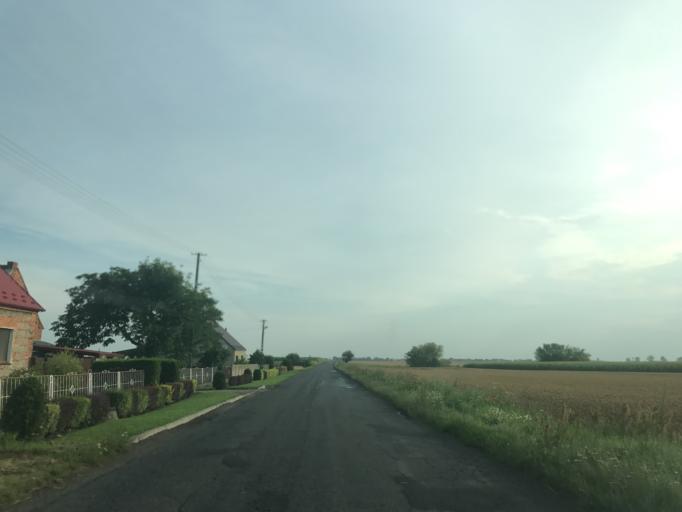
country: PL
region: Greater Poland Voivodeship
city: Miejska Gorka
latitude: 51.6383
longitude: 16.9609
